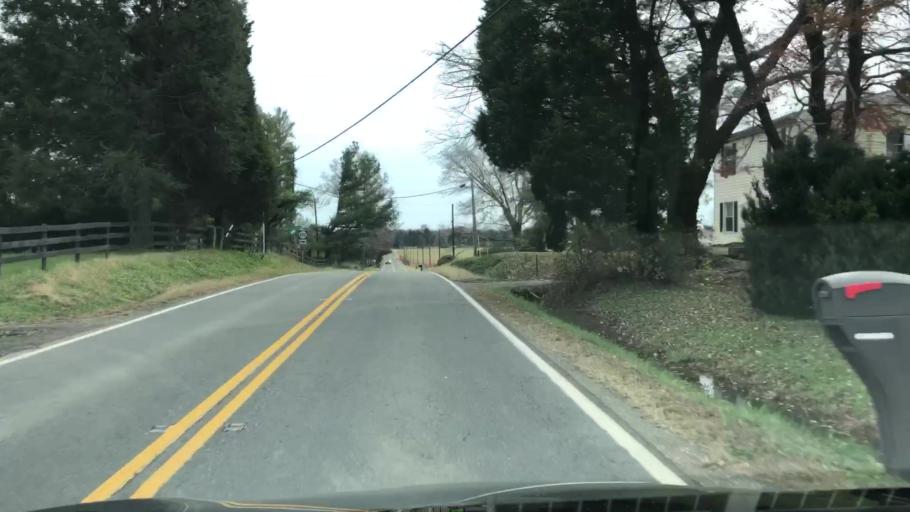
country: US
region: Virginia
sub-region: Fauquier County
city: New Baltimore
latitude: 38.7628
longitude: -77.6801
